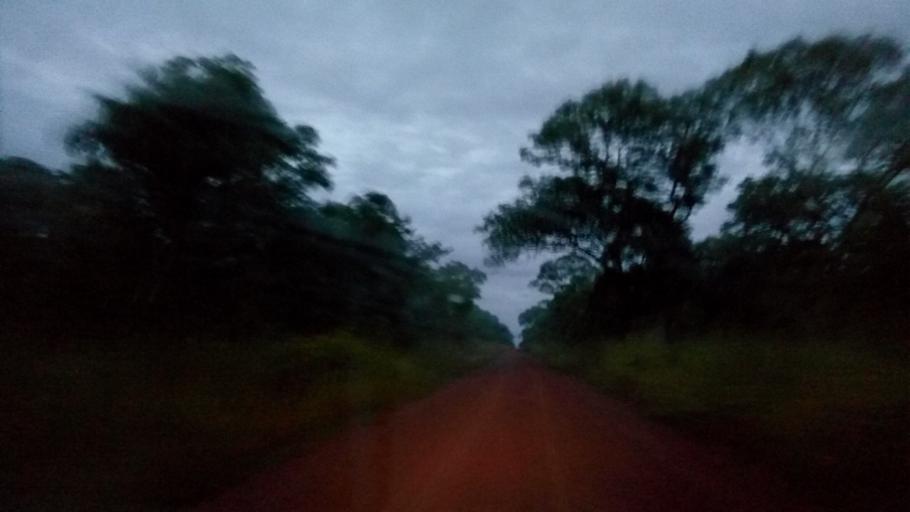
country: ZM
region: Luapula
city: Nchelenge
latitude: -9.7940
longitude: 28.1536
